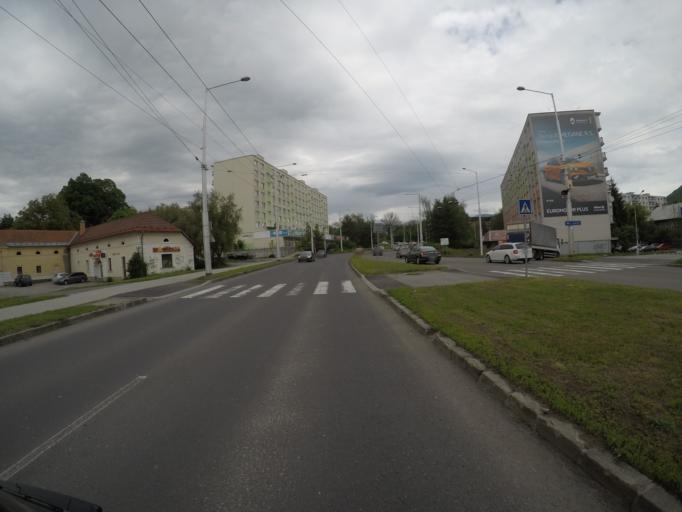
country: SK
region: Banskobystricky
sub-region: Okres Banska Bystrica
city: Banska Bystrica
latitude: 48.7223
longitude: 19.1321
